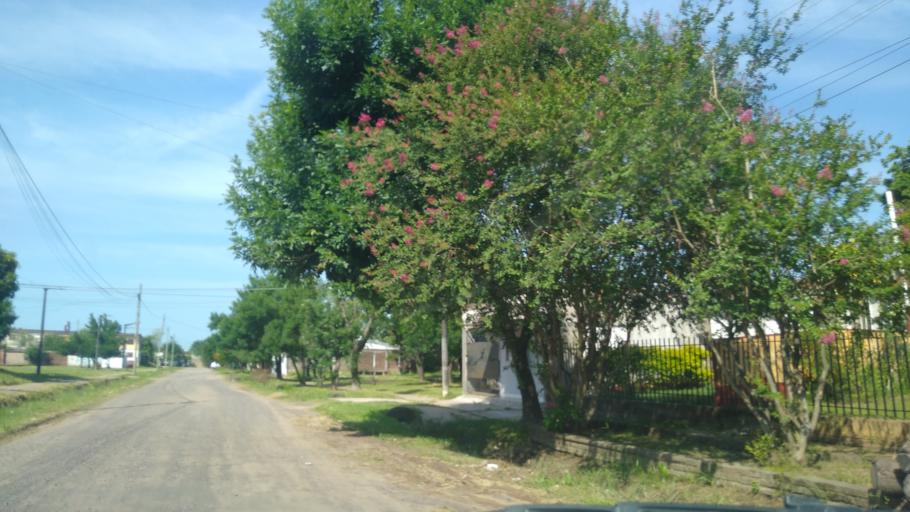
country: AR
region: Chaco
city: Puerto Vilelas
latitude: -27.4995
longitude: -58.9582
